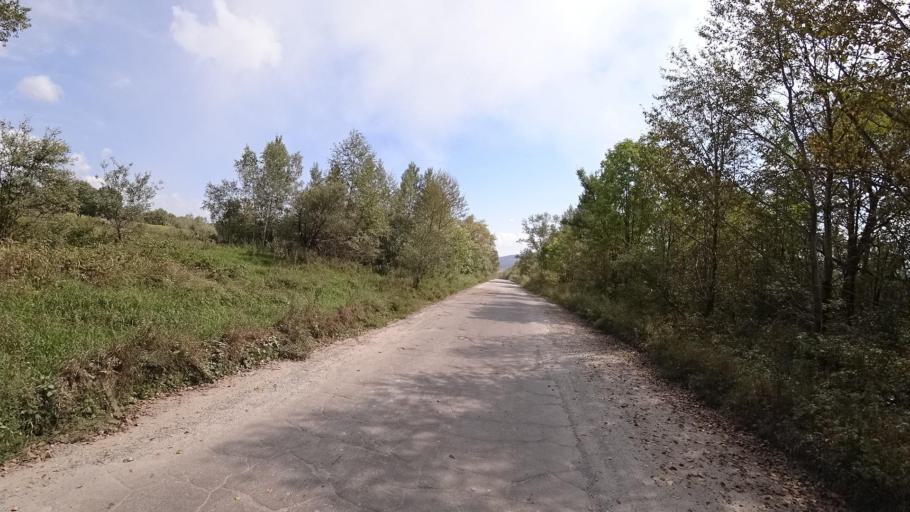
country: RU
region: Jewish Autonomous Oblast
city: Londoko
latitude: 49.0099
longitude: 131.9002
